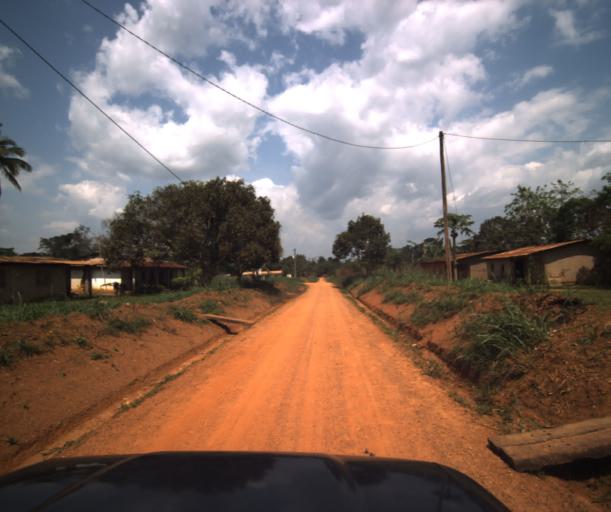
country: CM
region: Centre
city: Akono
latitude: 3.5578
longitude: 11.0656
